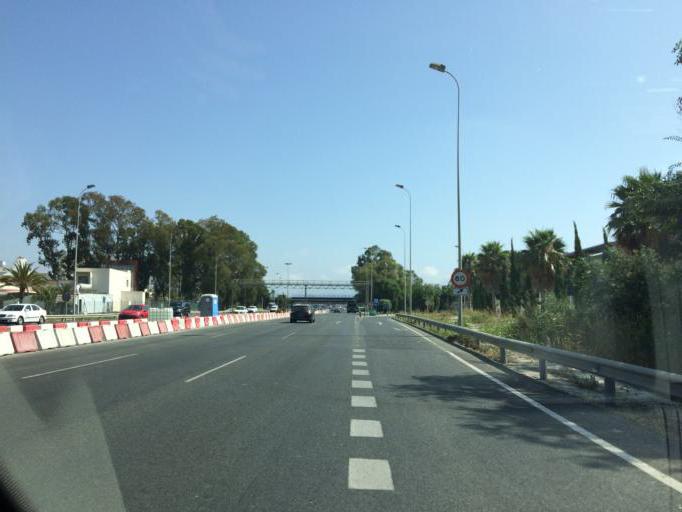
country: ES
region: Andalusia
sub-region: Provincia de Malaga
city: Torremolinos
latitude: 36.6679
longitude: -4.4804
